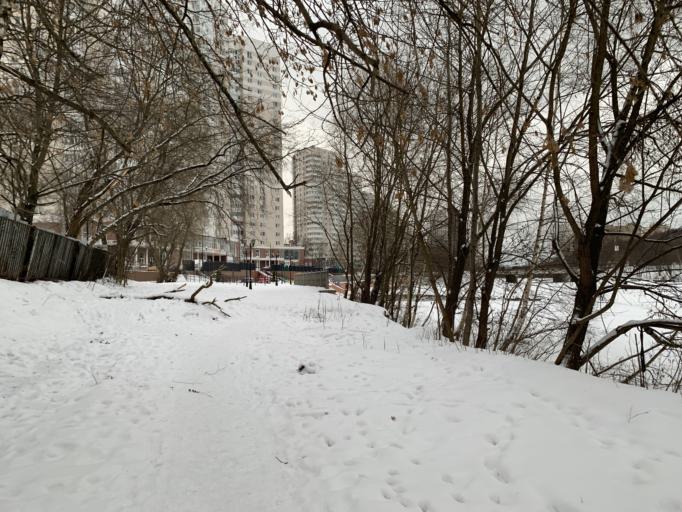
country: RU
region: Moskovskaya
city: Pushkino
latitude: 56.0082
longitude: 37.8577
